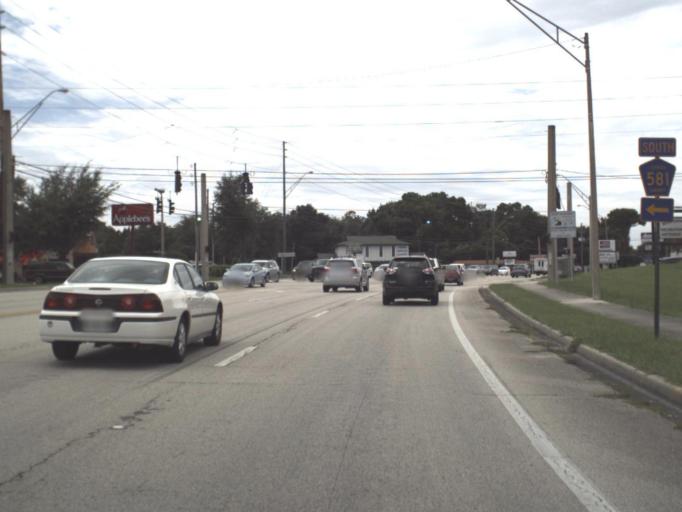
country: US
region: Florida
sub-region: Citrus County
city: Inverness
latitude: 28.8361
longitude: -82.3521
